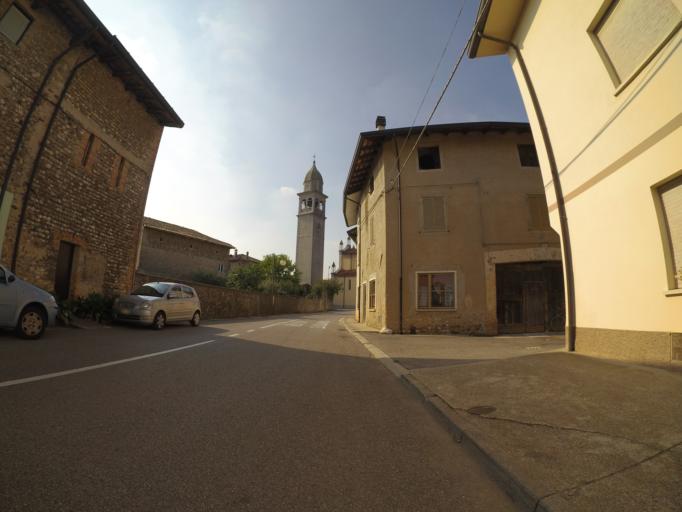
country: IT
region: Friuli Venezia Giulia
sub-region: Provincia di Udine
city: Basiliano
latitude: 45.9961
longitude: 13.0268
